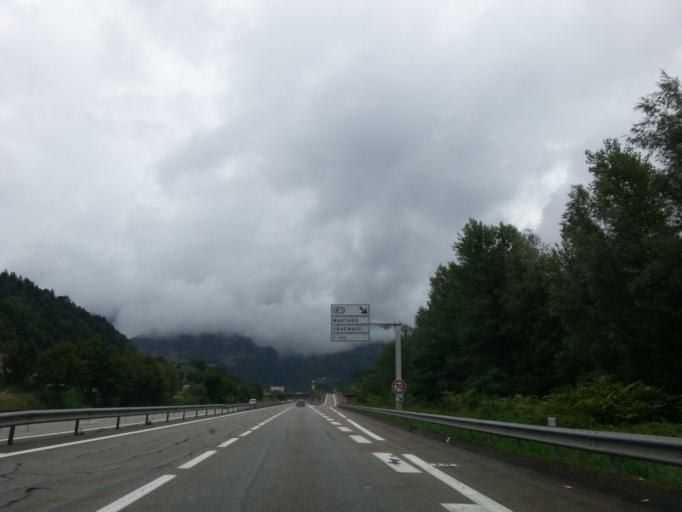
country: FR
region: Rhone-Alpes
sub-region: Departement de la Savoie
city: Marthod
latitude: 45.7275
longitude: 6.4166
